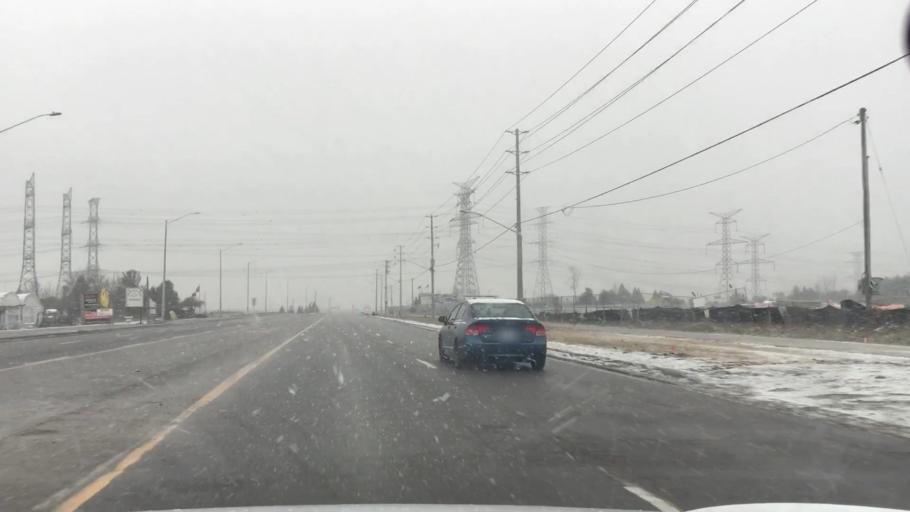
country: CA
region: Ontario
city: Ajax
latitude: 43.8714
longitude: -79.0843
